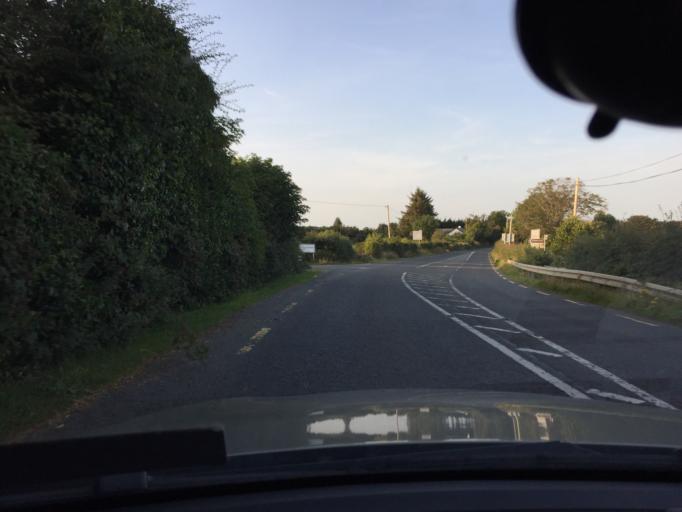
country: IE
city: Newtownmountkennedy
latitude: 53.0896
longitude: -6.2077
